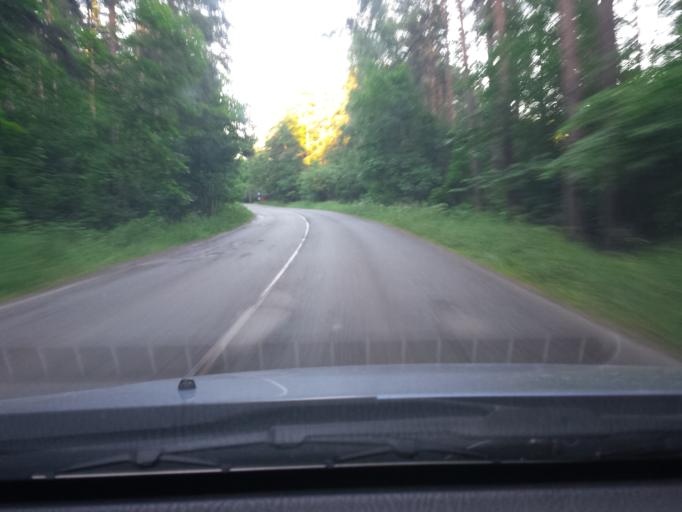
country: LV
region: Riga
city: Bergi
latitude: 57.0052
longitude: 24.2492
